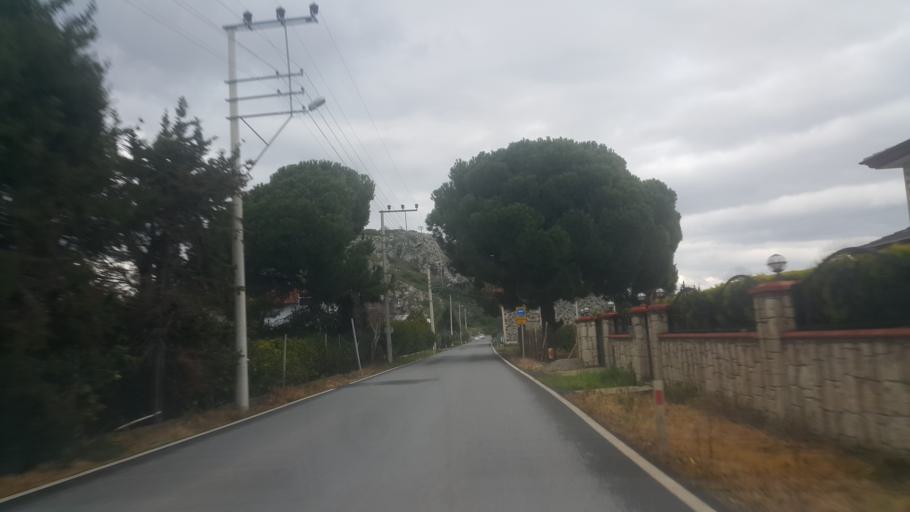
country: TR
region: Izmir
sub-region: Seferihisar
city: Seferhisar
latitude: 38.1906
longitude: 26.8031
